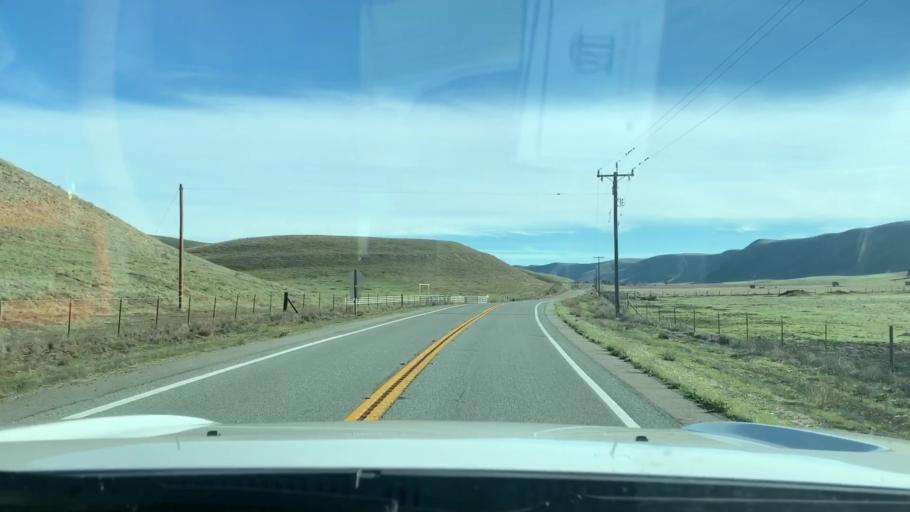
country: US
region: California
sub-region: Monterey County
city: King City
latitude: 36.1488
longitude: -120.9626
